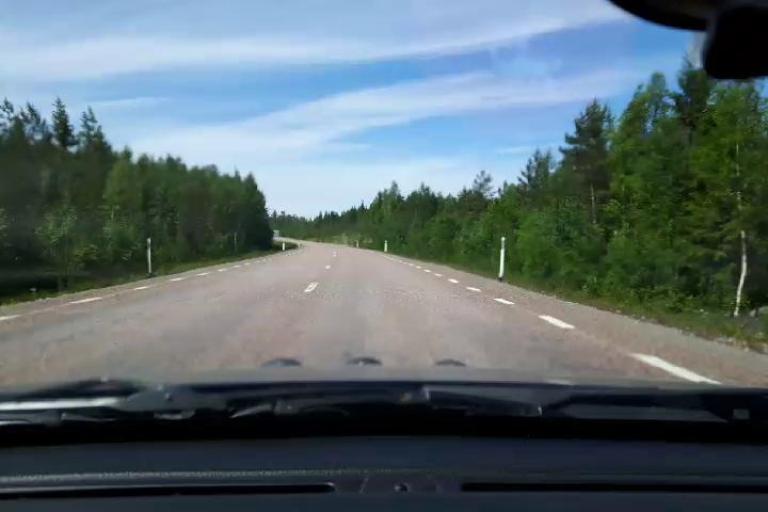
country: SE
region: Gaevleborg
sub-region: Gavle Kommun
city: Norrsundet
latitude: 61.0783
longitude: 16.9628
